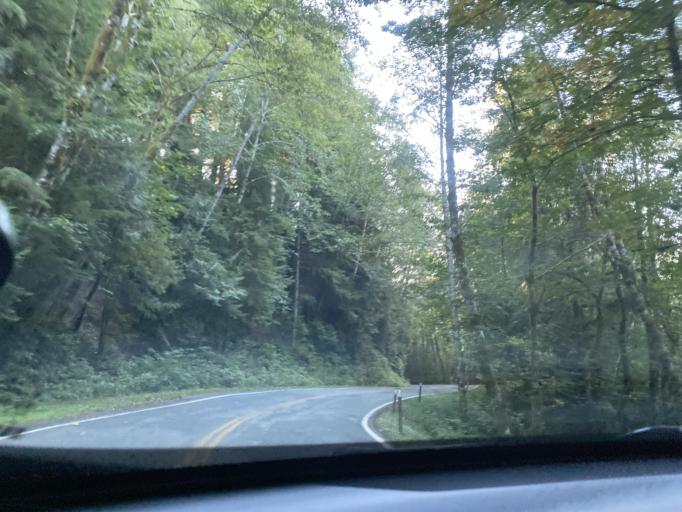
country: US
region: Washington
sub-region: Clallam County
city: Forks
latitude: 47.8233
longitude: -124.2027
